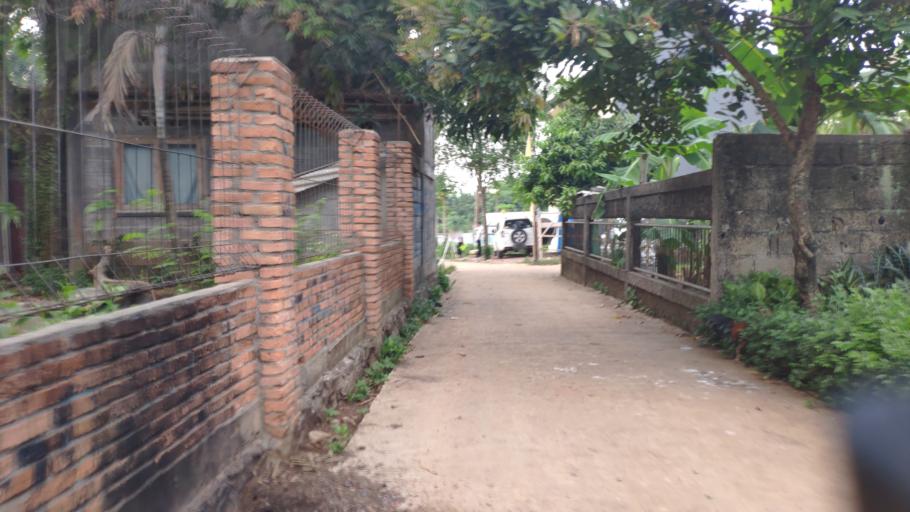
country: ID
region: West Java
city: Pamulang
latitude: -6.3550
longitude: 106.7724
